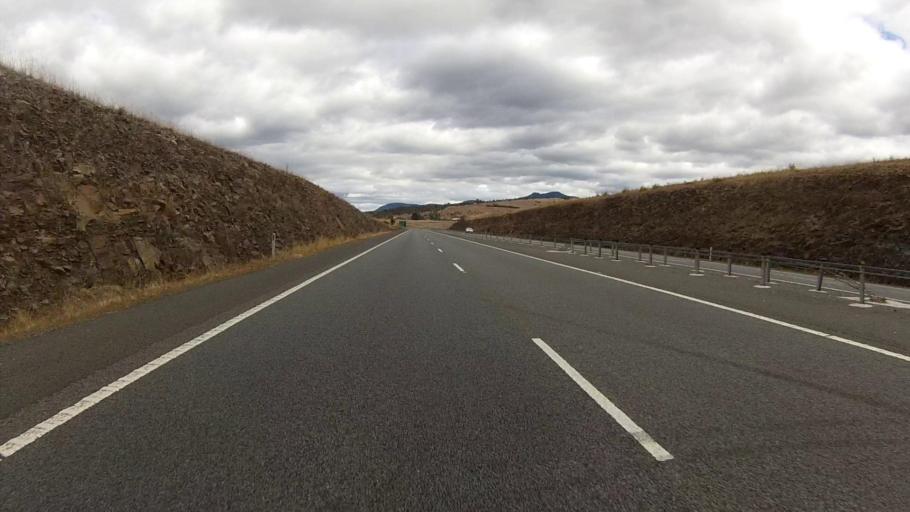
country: AU
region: Tasmania
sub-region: Brighton
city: Bridgewater
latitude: -42.7072
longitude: 147.2578
